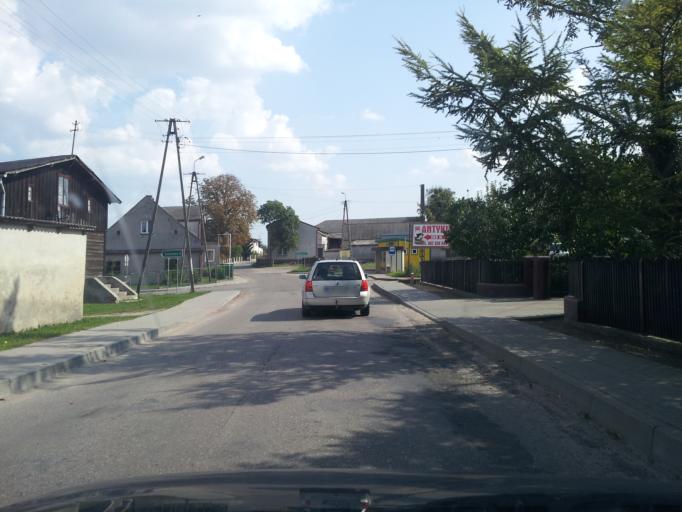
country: PL
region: Kujawsko-Pomorskie
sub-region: Powiat brodnicki
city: Swiedziebnia
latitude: 53.2156
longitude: 19.5200
